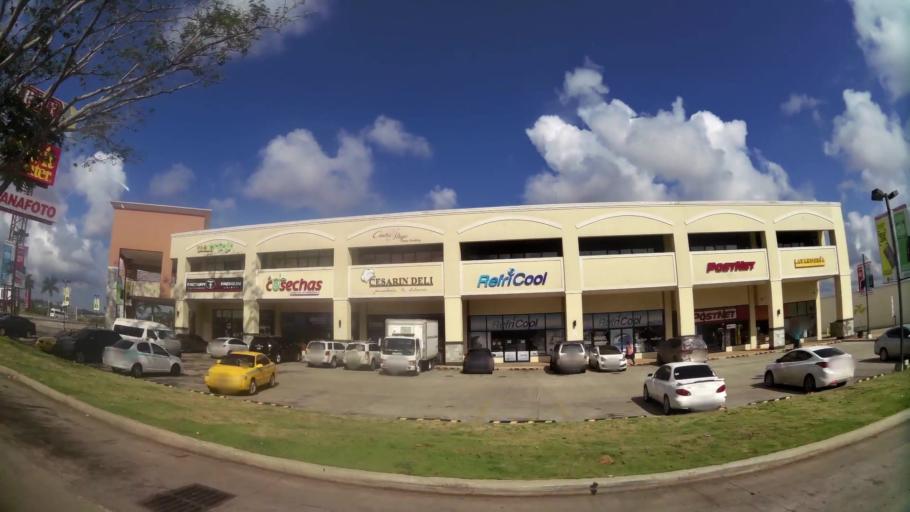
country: PA
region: Panama
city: La Chorrera
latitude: 8.8921
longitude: -79.7502
